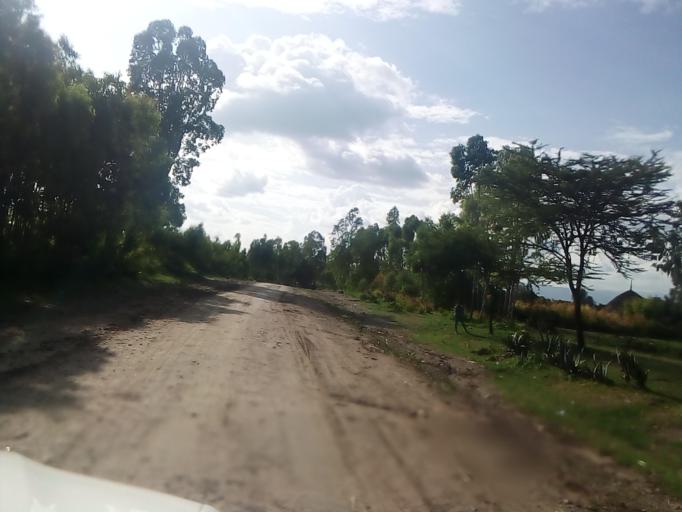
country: ET
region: Southern Nations, Nationalities, and People's Region
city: K'olito
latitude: 7.6411
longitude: 38.0564
